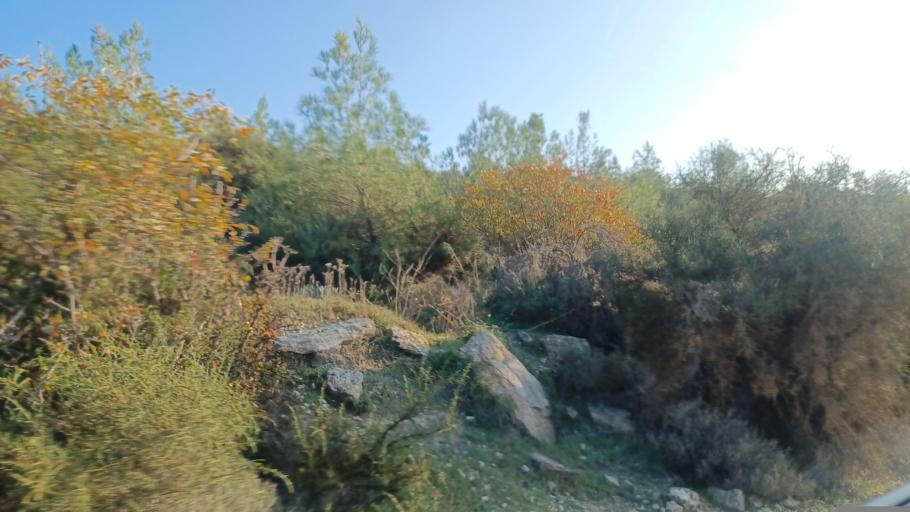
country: CY
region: Larnaka
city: Kofinou
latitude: 34.8185
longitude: 33.3162
